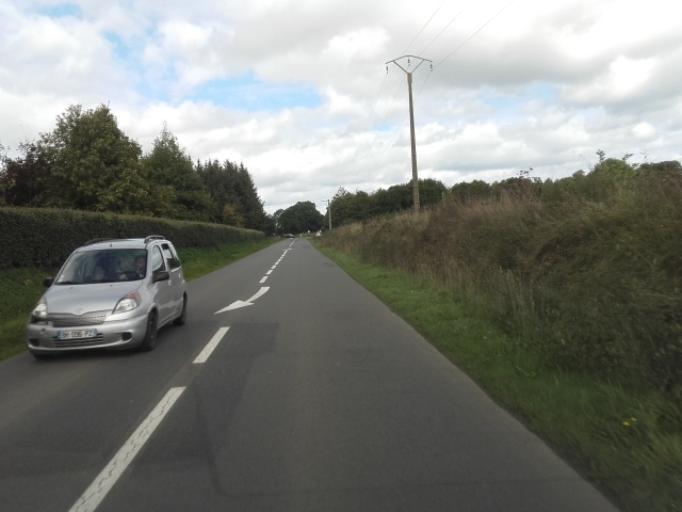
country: FR
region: Brittany
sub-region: Departement des Cotes-d'Armor
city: Lanvollon
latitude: 48.6370
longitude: -2.9757
